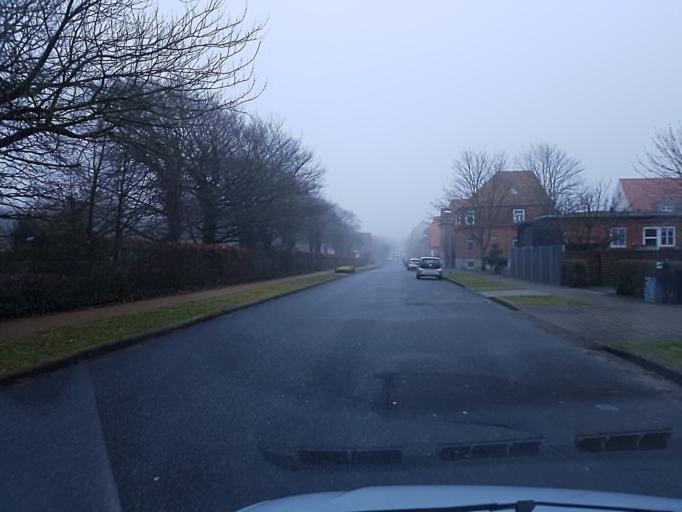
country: DK
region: South Denmark
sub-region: Esbjerg Kommune
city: Esbjerg
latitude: 55.4763
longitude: 8.4418
